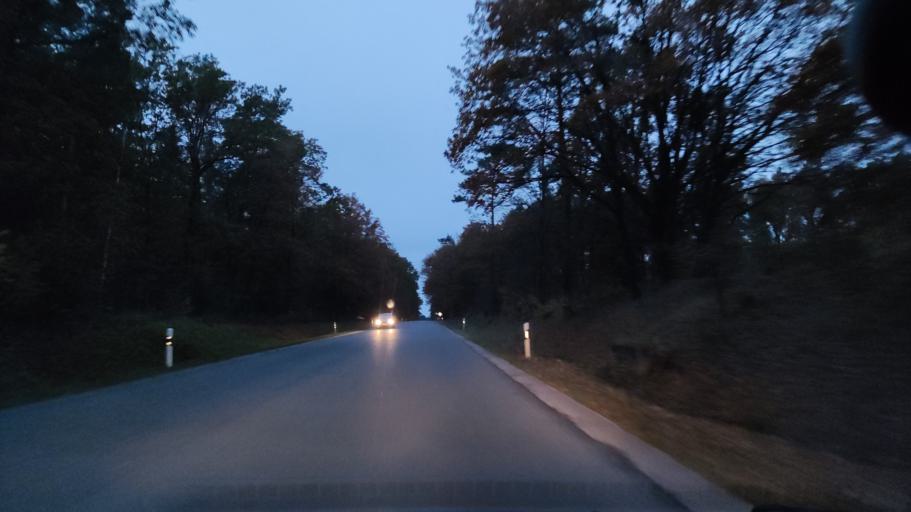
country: DE
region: Lower Saxony
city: Munster
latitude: 53.0080
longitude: 10.1085
